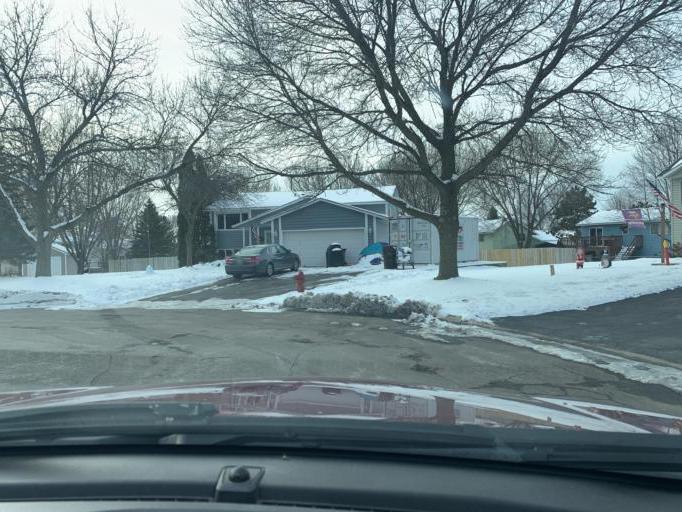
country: US
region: Minnesota
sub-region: Washington County
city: Saint Paul Park
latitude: 44.8291
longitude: -92.9857
